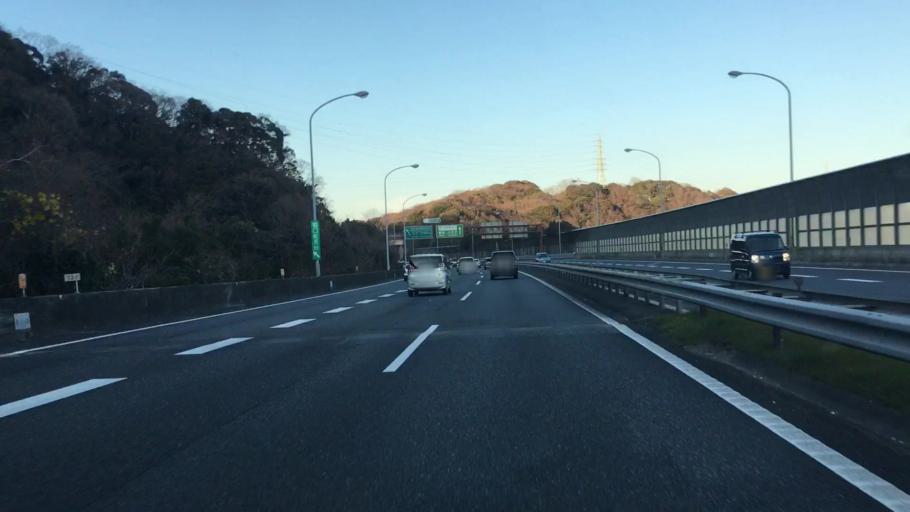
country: JP
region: Kanagawa
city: Zushi
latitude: 35.3439
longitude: 139.5920
